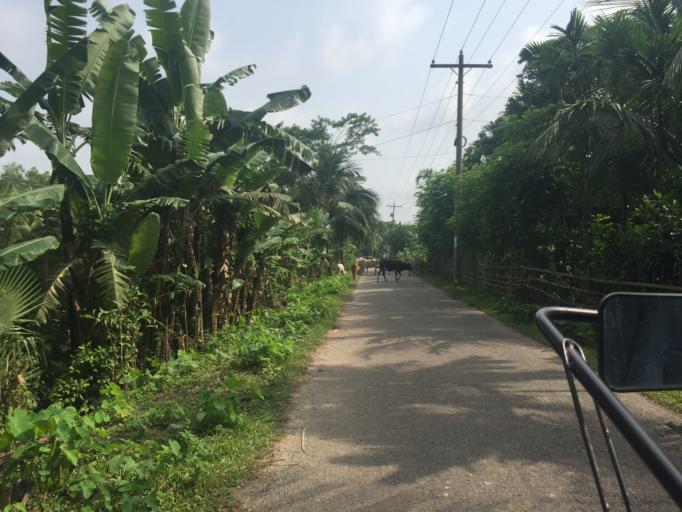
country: BD
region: Barisal
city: Mathba
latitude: 22.2294
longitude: 89.9158
